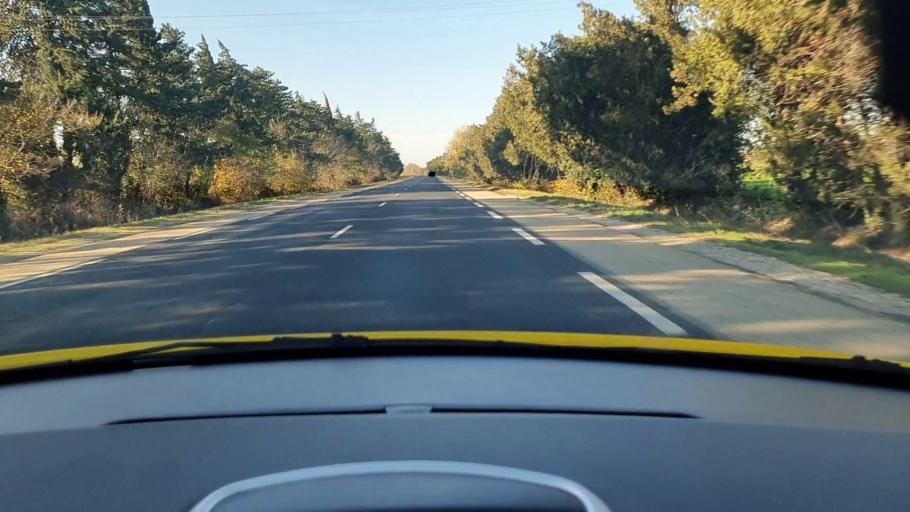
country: FR
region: Languedoc-Roussillon
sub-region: Departement du Gard
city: Fourques
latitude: 43.7017
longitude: 4.5724
